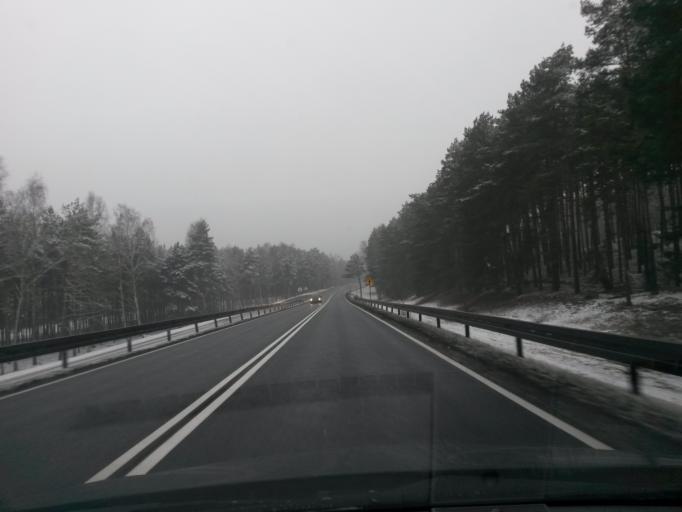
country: PL
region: Kujawsko-Pomorskie
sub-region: Powiat bydgoski
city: Nowa Wies Wielka
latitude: 53.0612
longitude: 18.0875
